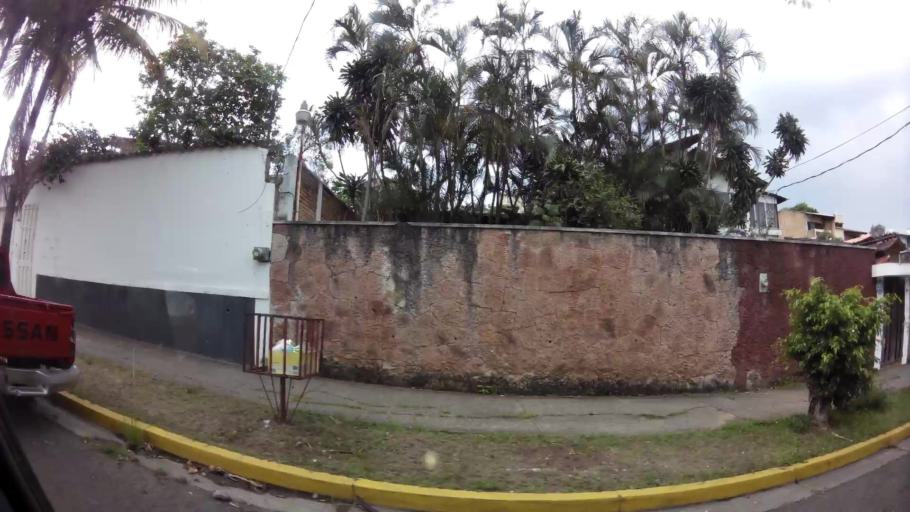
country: HN
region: Francisco Morazan
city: Tegucigalpa
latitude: 14.0932
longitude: -87.1759
